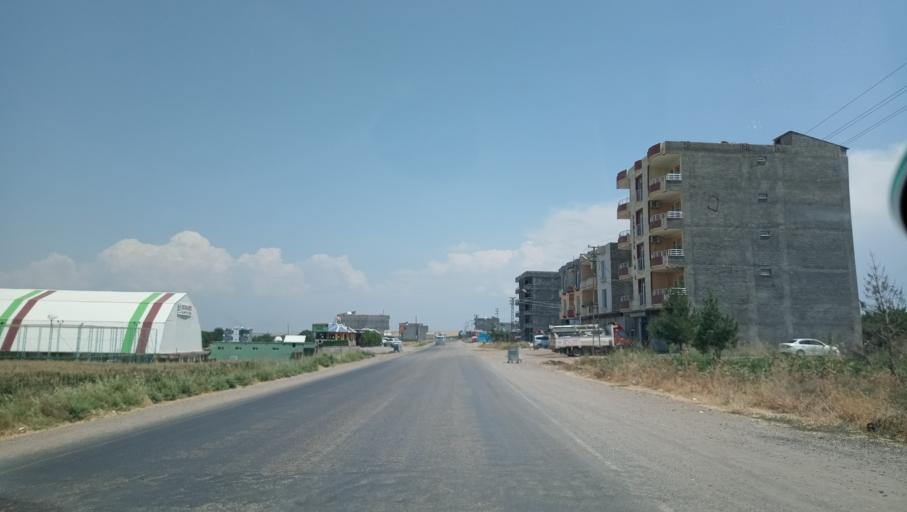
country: TR
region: Diyarbakir
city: Aralik
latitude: 37.8281
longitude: 40.6746
